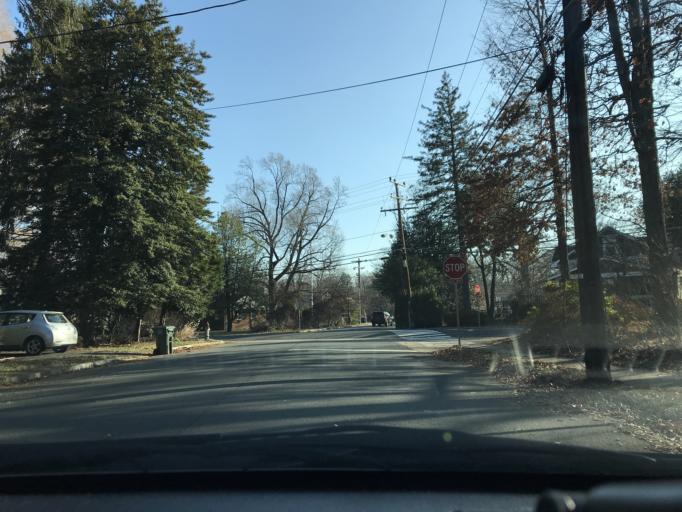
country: US
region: Virginia
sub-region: City of Falls Church
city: Falls Church
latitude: 38.8919
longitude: -77.1778
